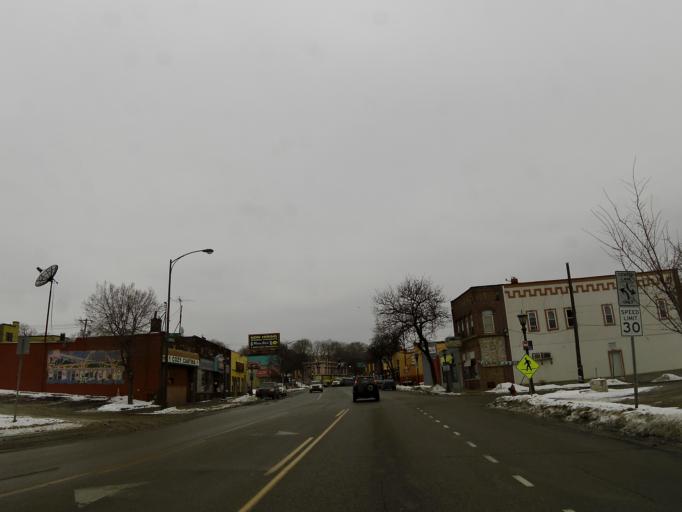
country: US
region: Minnesota
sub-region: Ramsey County
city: Saint Paul
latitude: 44.9294
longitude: -93.0764
